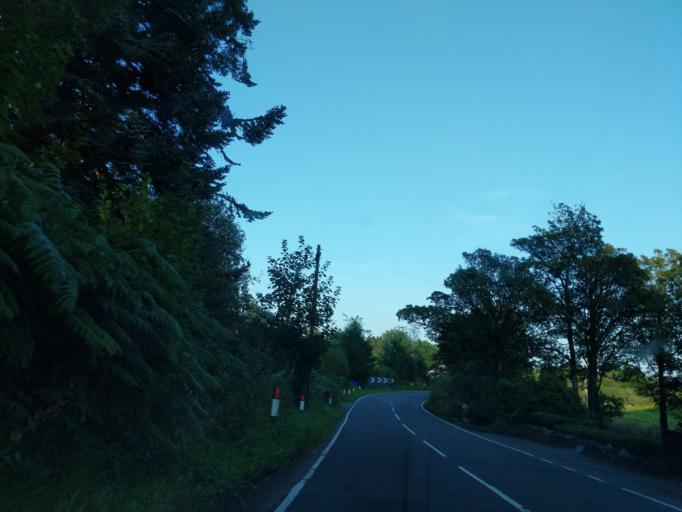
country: GB
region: Scotland
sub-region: Stirling
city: Balfron
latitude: 56.1779
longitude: -4.3226
